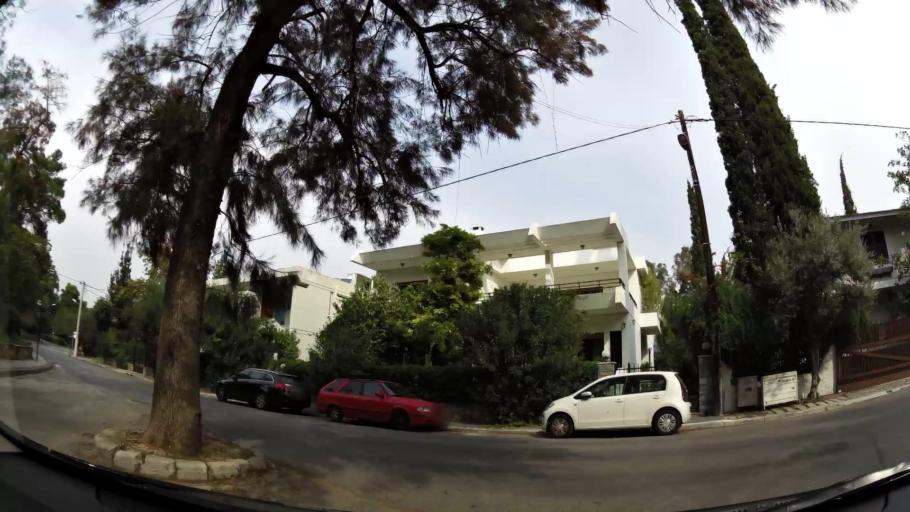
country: GR
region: Attica
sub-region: Nomarchia Athinas
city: Filothei
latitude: 38.0256
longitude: 23.7806
